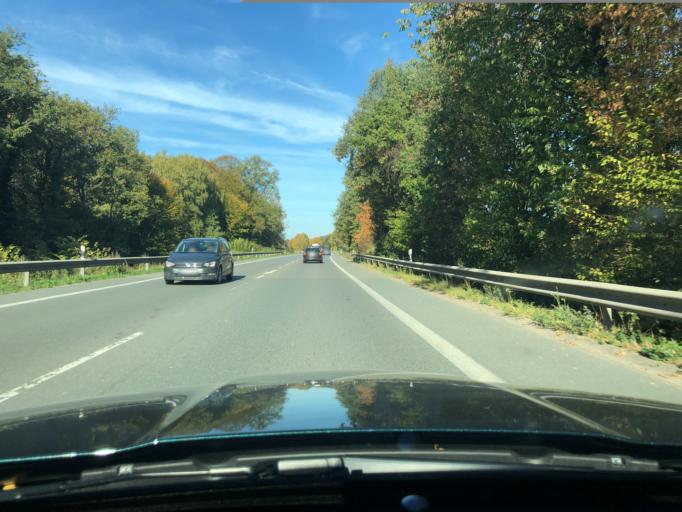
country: DE
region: North Rhine-Westphalia
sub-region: Regierungsbezirk Munster
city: Greven
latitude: 52.0615
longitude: 7.6736
